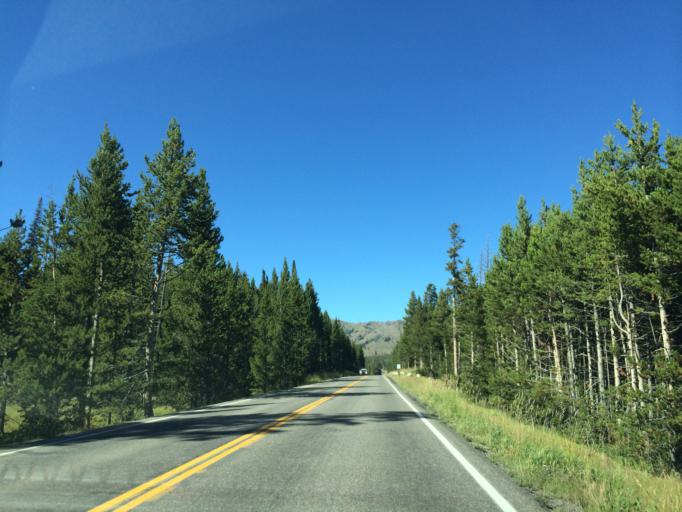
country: US
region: Montana
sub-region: Gallatin County
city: West Yellowstone
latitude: 44.7288
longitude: -110.4938
